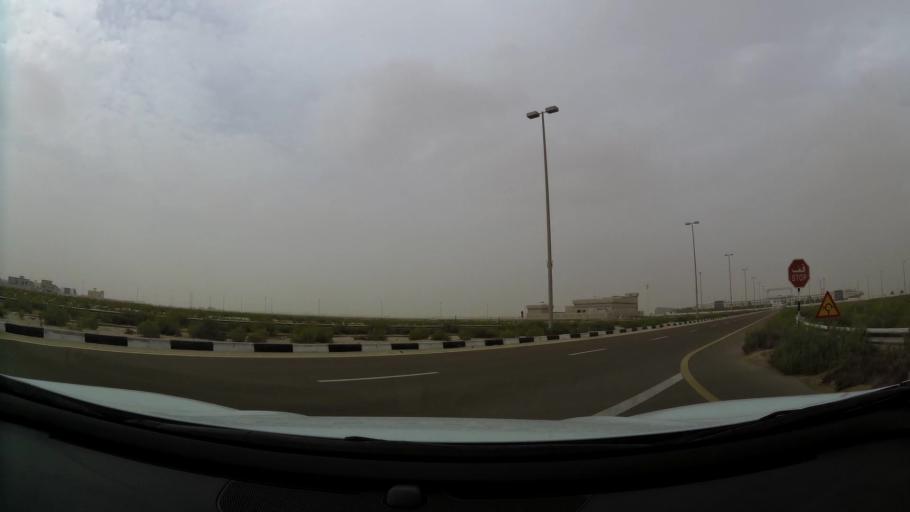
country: AE
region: Abu Dhabi
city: Abu Dhabi
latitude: 24.3688
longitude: 54.6889
